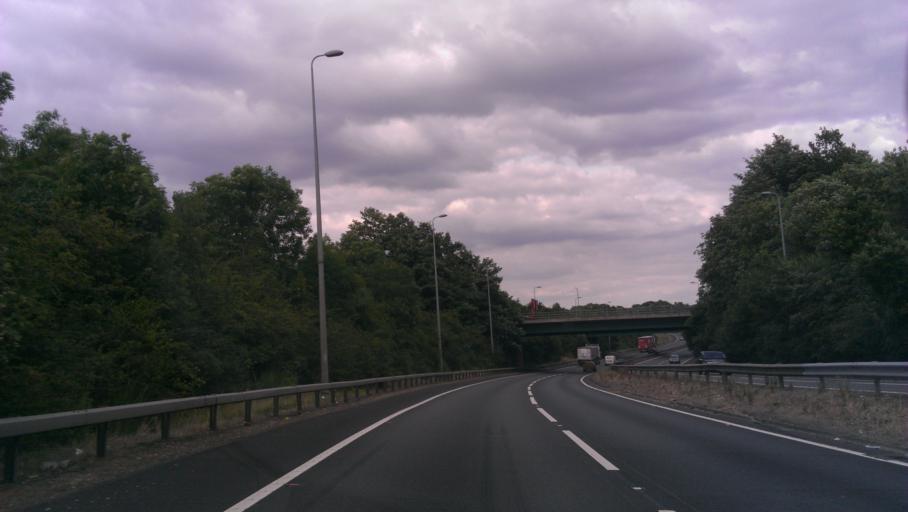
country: GB
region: England
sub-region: Essex
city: Brentwood
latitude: 51.6456
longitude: 0.3412
